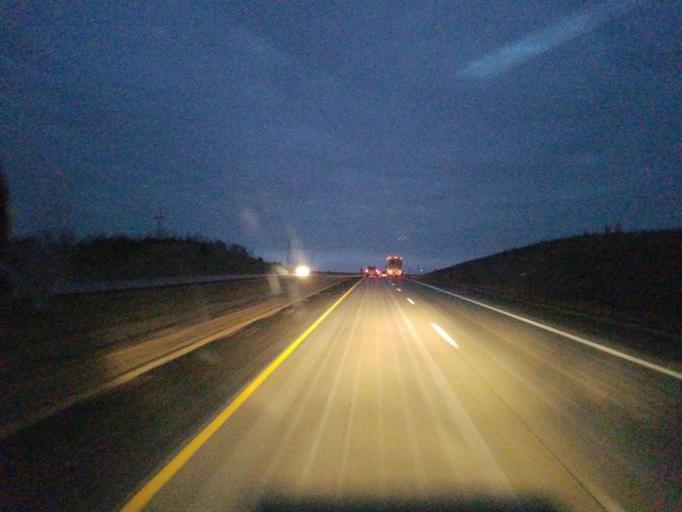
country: US
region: Iowa
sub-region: Guthrie County
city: Guthrie Center
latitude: 41.4968
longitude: -94.7127
